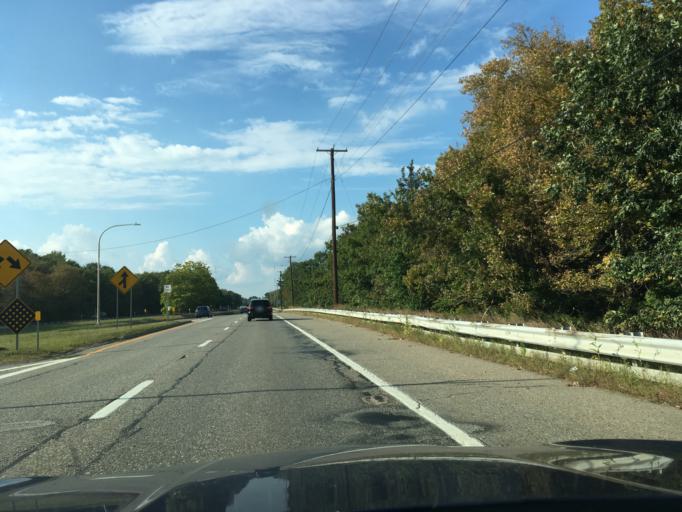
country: US
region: Rhode Island
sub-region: Bristol County
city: Barrington
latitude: 41.7672
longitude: -71.3221
